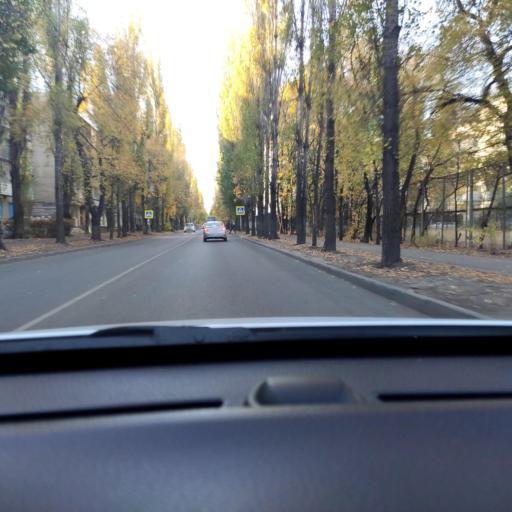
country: RU
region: Voronezj
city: Voronezh
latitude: 51.6854
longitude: 39.2574
